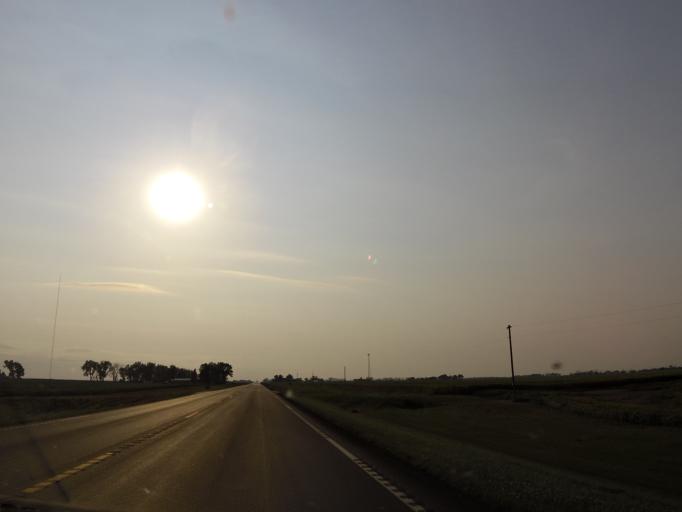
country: US
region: North Dakota
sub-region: Traill County
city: Mayville
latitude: 47.3529
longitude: -97.2502
